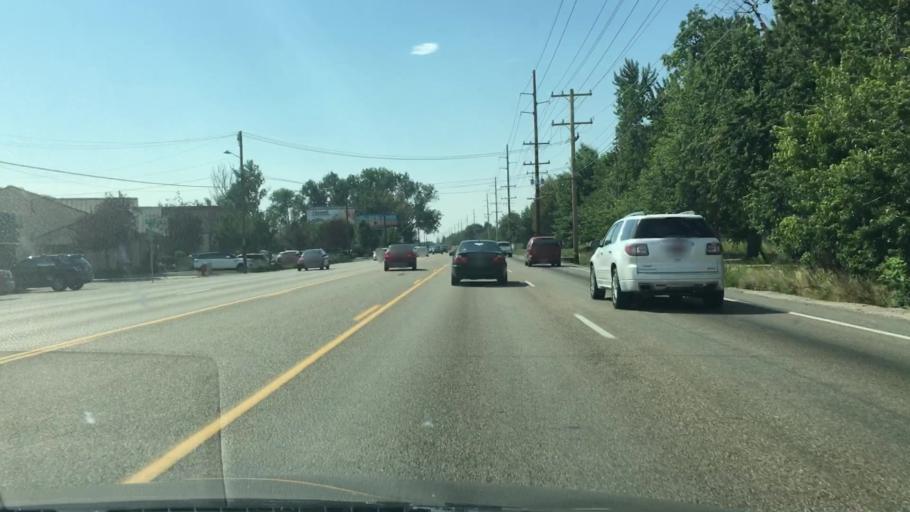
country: US
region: Idaho
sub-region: Ada County
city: Eagle
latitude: 43.6770
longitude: -116.2981
